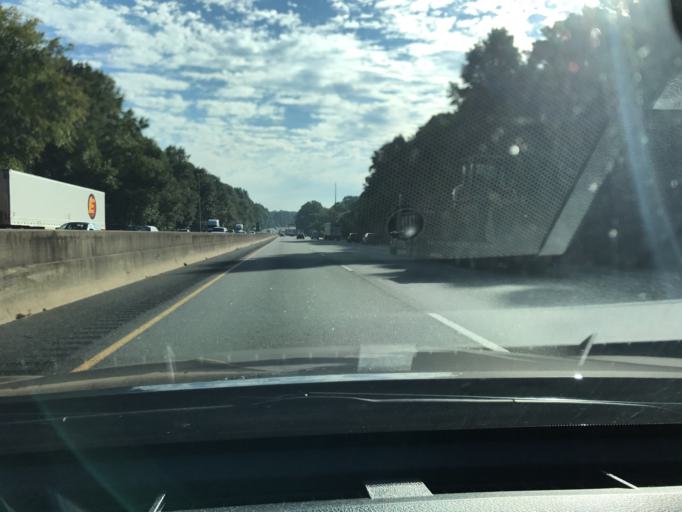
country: US
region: Georgia
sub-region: DeKalb County
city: Panthersville
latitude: 33.6941
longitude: -84.2905
